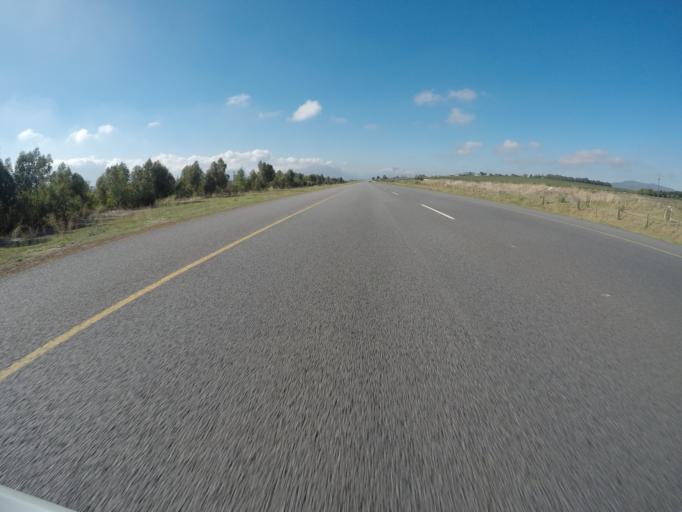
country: ZA
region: Western Cape
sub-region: City of Cape Town
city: Kraaifontein
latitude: -33.8532
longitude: 18.8068
